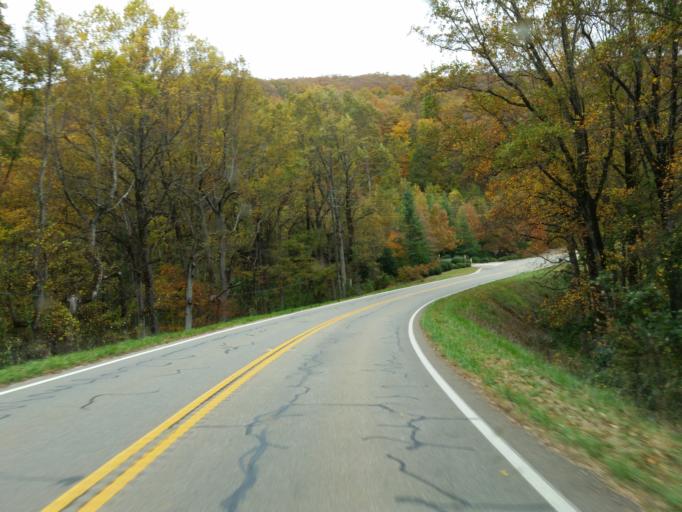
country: US
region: Georgia
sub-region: Pickens County
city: Jasper
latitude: 34.5339
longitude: -84.3908
